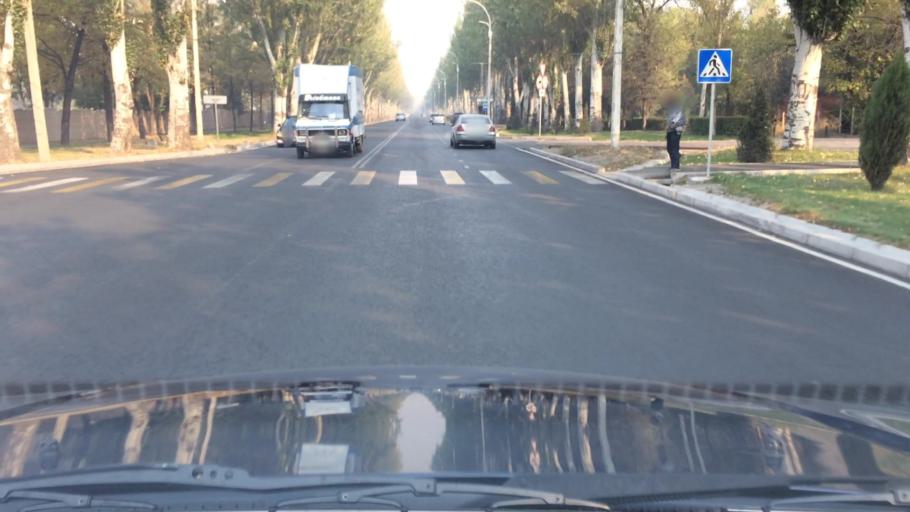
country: KG
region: Chuy
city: Bishkek
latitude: 42.8319
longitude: 74.5854
